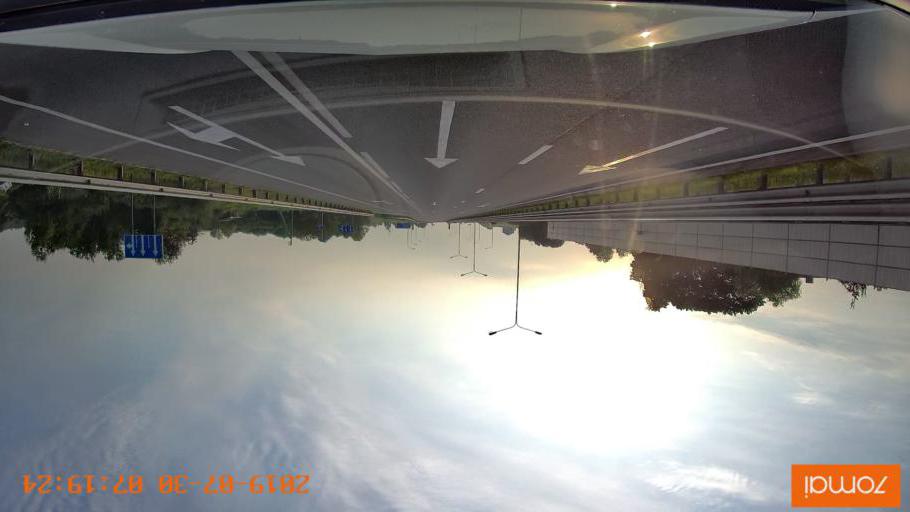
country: RU
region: Kaliningrad
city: Bol'shoe Isakovo
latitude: 54.7012
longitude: 20.6740
